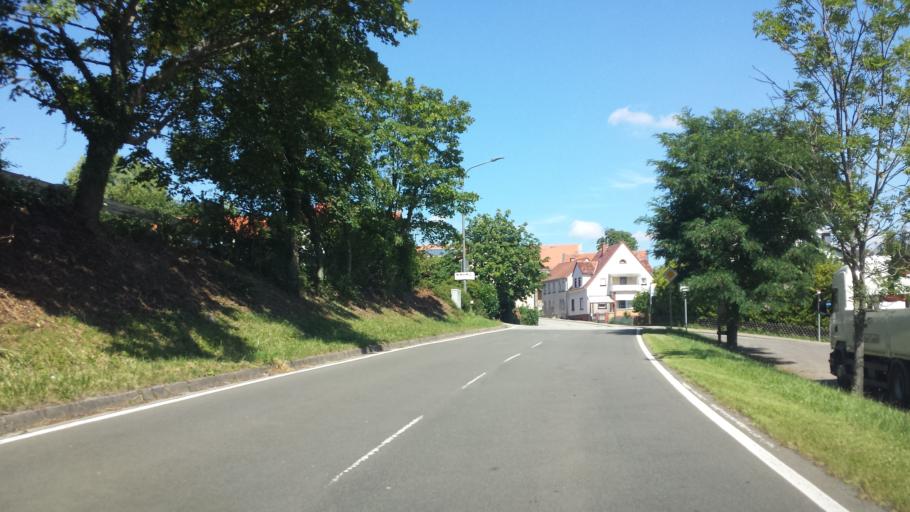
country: DE
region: Rheinland-Pfalz
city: Dannenfels
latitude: 49.6259
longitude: 7.9473
